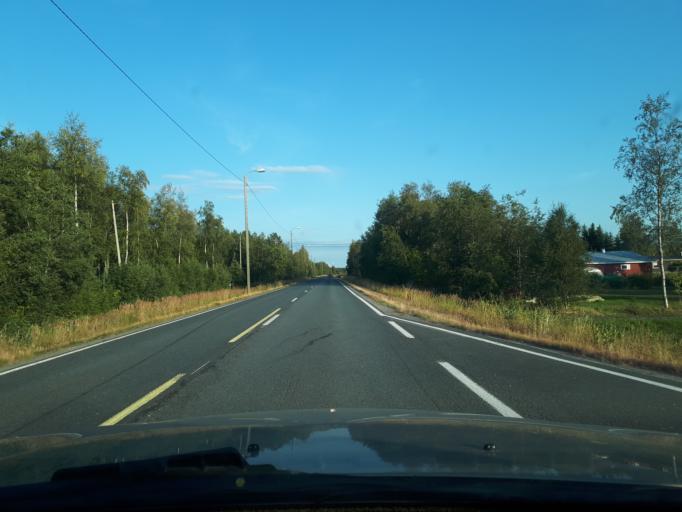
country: FI
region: Northern Ostrobothnia
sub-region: Oulu
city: Oulunsalo
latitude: 64.9853
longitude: 25.2641
